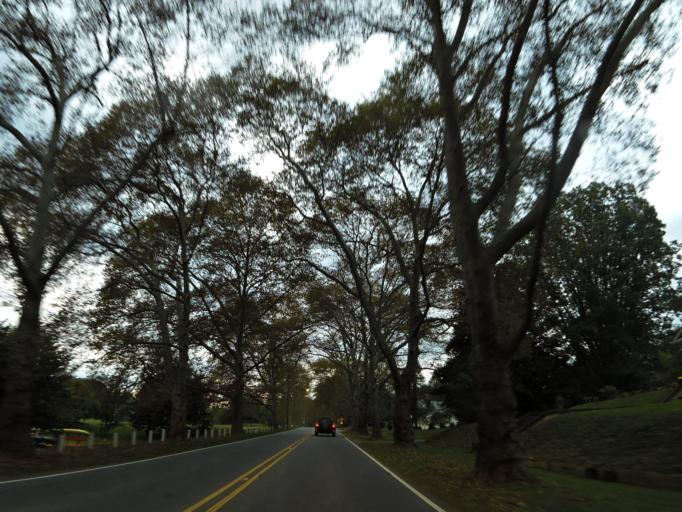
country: US
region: North Carolina
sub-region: Buncombe County
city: Woodfin
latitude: 35.6360
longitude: -82.5653
